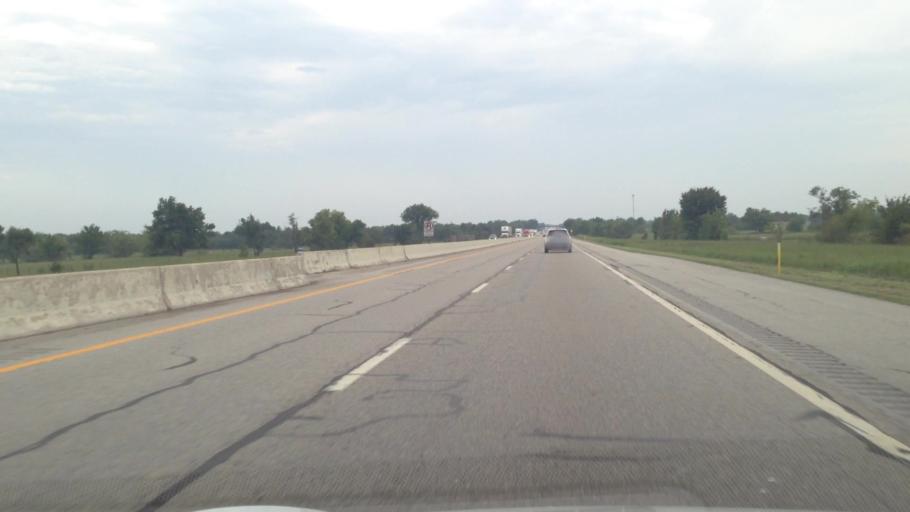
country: US
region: Oklahoma
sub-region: Ottawa County
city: Fairland
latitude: 36.7922
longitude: -94.8845
